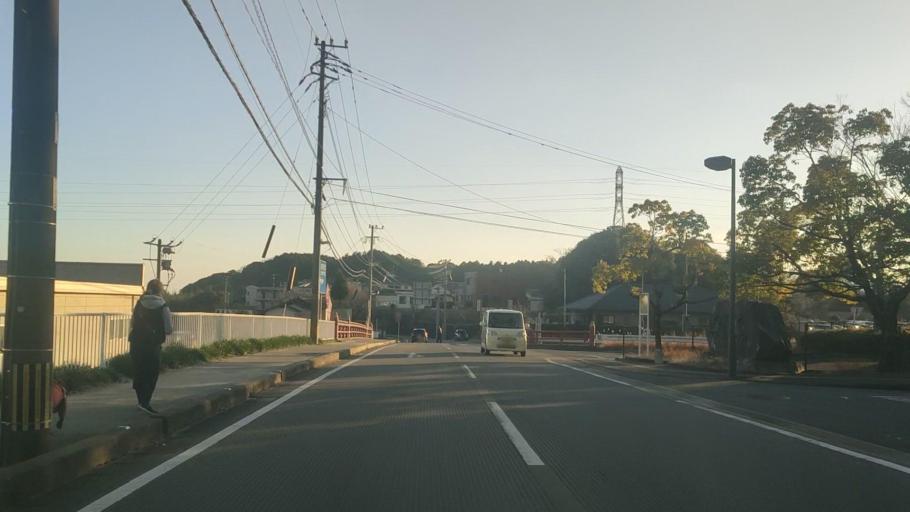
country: JP
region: Fukuoka
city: Dazaifu
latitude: 33.5270
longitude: 130.5435
